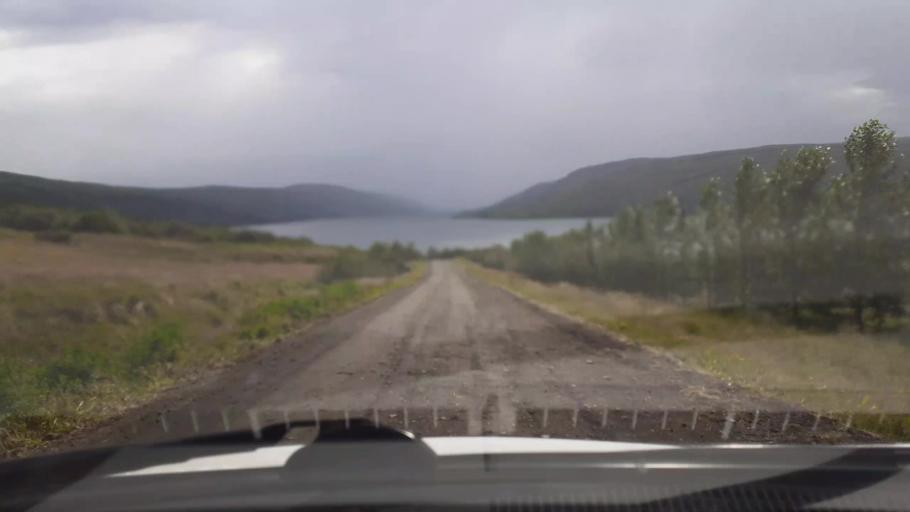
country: IS
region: Capital Region
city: Mosfellsbaer
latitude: 64.5231
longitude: -21.4709
